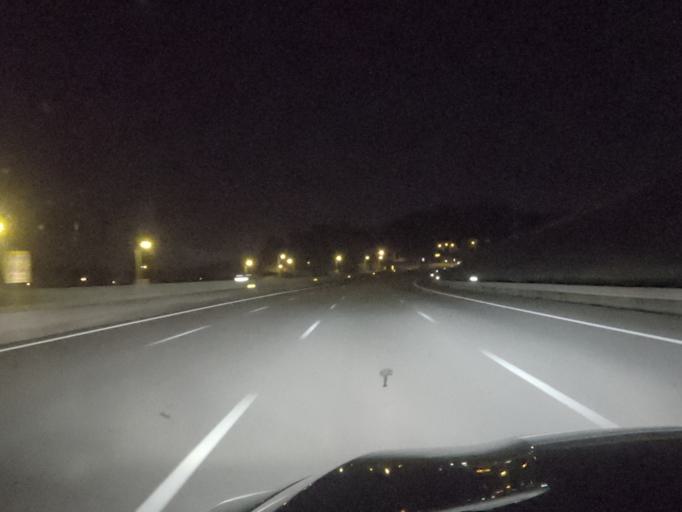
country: PT
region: Porto
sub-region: Vila Nova de Gaia
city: Grijo
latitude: 41.0444
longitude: -8.5706
